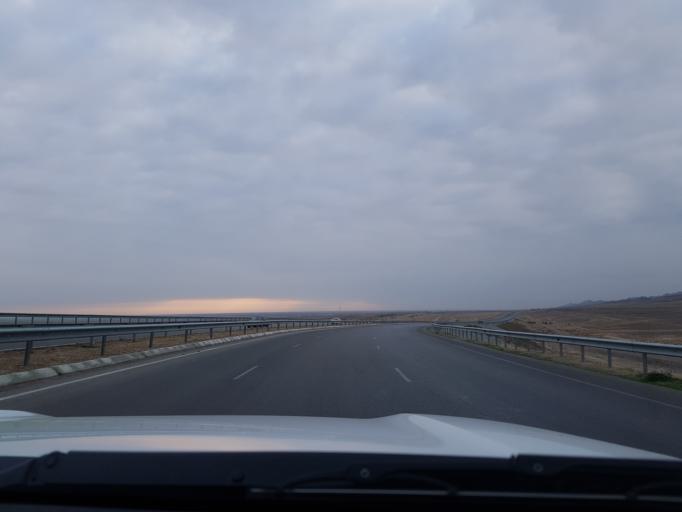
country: IR
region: Razavi Khorasan
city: Dargaz
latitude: 37.6825
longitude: 59.0824
